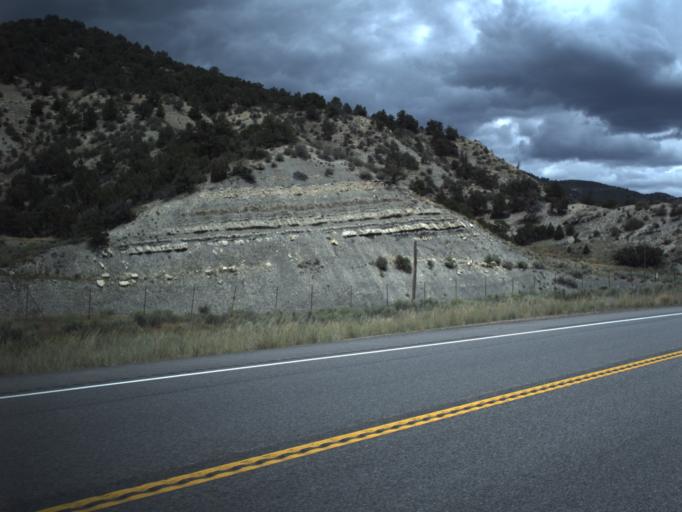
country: US
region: Utah
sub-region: Carbon County
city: Helper
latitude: 39.9313
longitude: -111.1673
